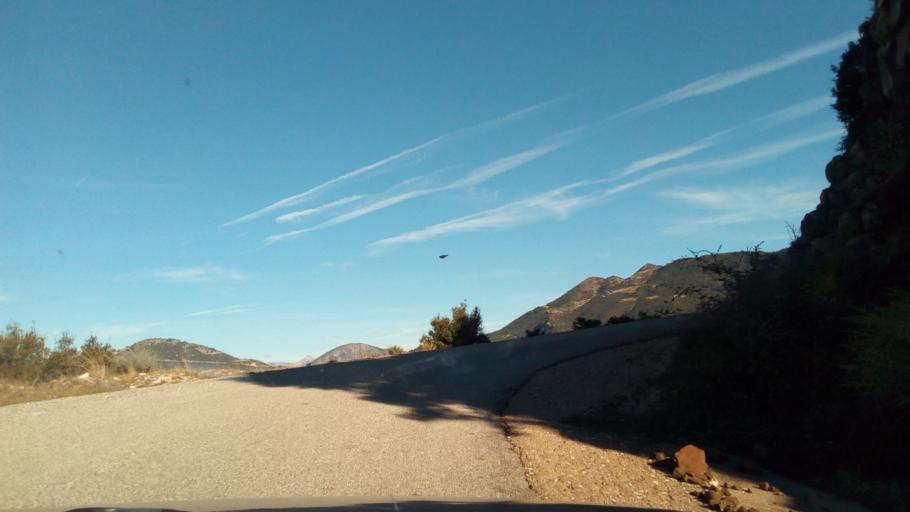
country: GR
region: West Greece
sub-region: Nomos Aitolias kai Akarnanias
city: Nafpaktos
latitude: 38.5084
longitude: 21.8365
